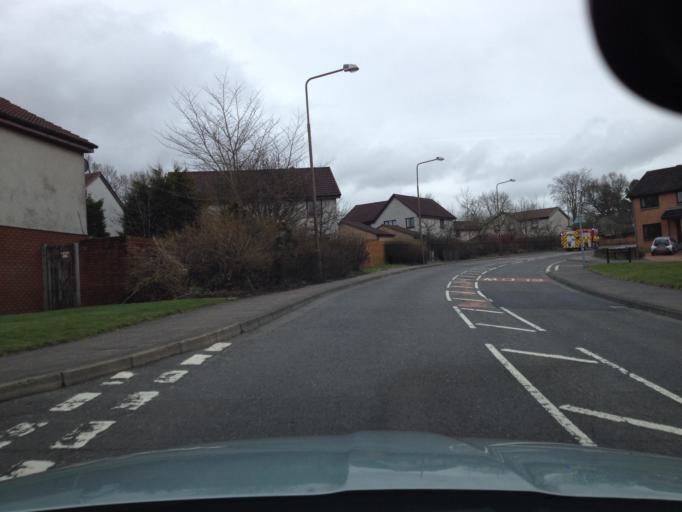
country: GB
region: Scotland
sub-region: West Lothian
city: Mid Calder
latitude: 55.8829
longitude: -3.4883
